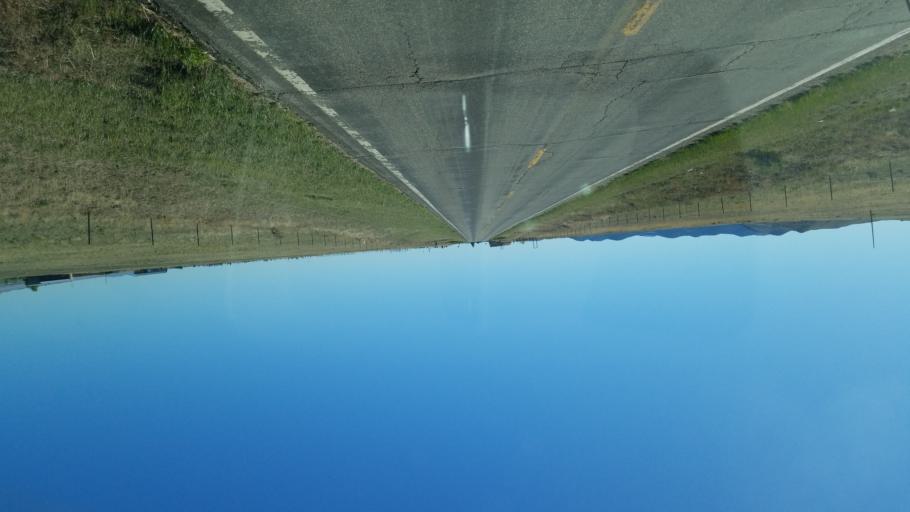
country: US
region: Colorado
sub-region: Custer County
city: Westcliffe
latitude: 38.1663
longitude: -105.4880
